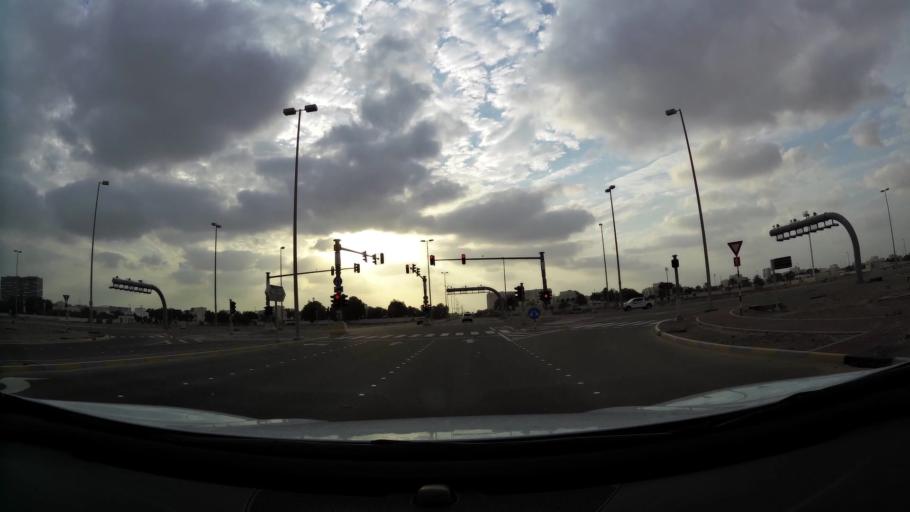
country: AE
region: Abu Dhabi
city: Abu Dhabi
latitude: 24.3834
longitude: 54.5363
